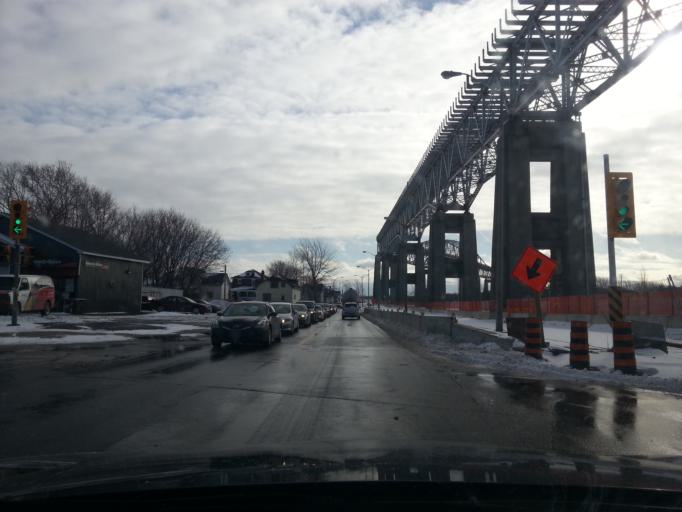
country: CA
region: Ontario
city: Cornwall
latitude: 45.0154
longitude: -74.7416
